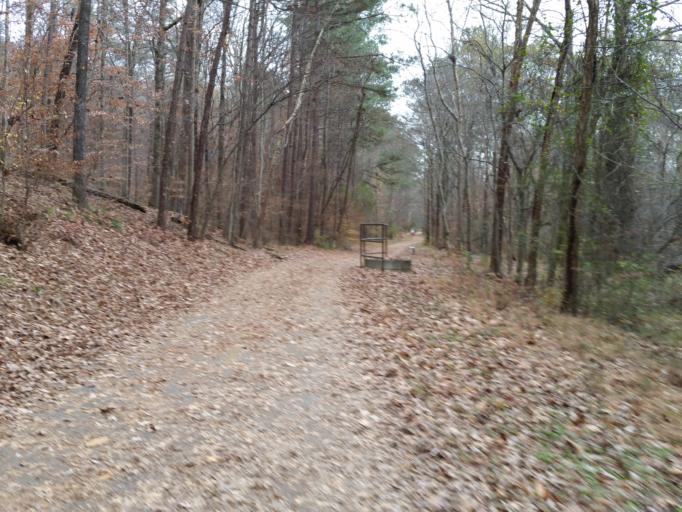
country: US
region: Georgia
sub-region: Cobb County
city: Vinings
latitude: 33.8794
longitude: -84.4503
